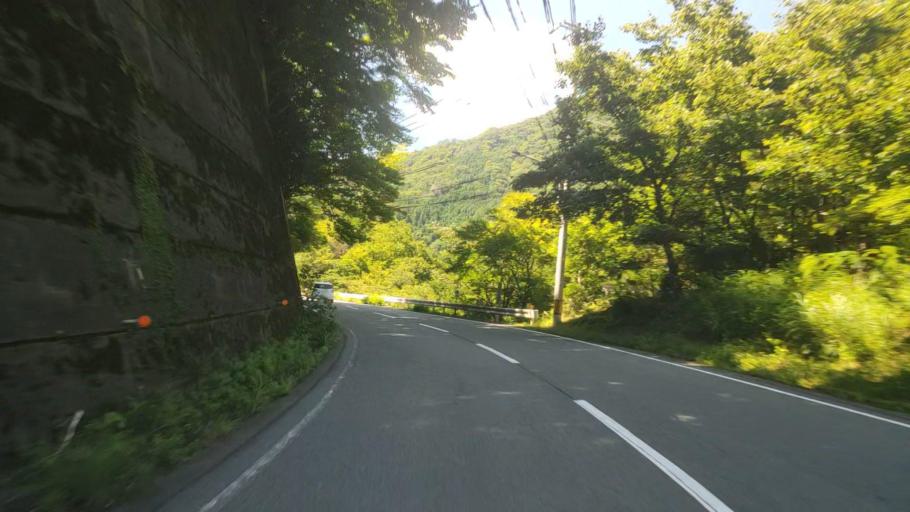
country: JP
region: Mie
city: Owase
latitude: 34.1890
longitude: 135.9958
